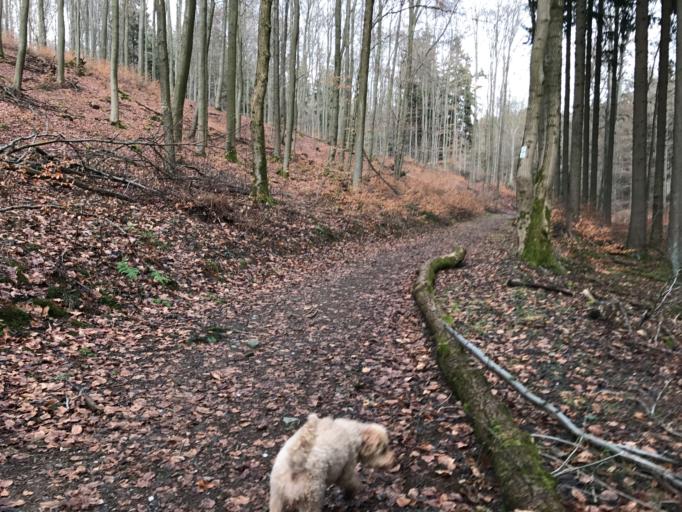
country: DE
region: Hesse
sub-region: Regierungsbezirk Darmstadt
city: Konigstein im Taunus
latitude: 50.2071
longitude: 8.4587
